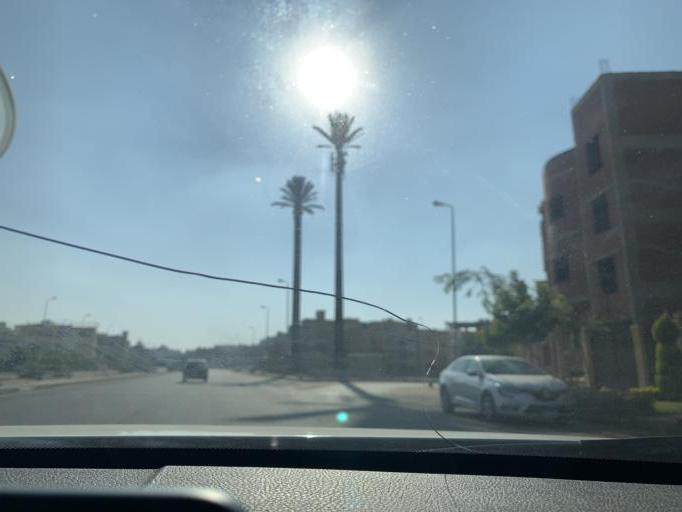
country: EG
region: Muhafazat al Qalyubiyah
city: Al Khankah
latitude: 30.0063
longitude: 31.4820
